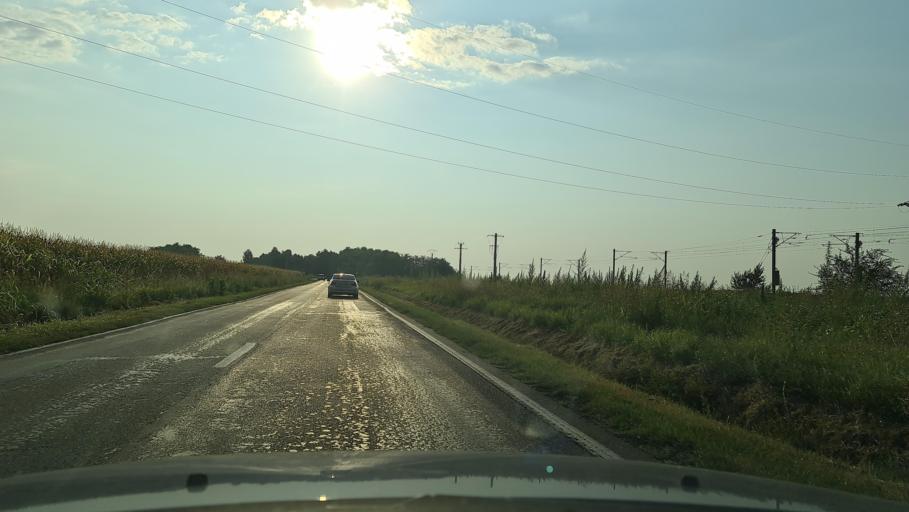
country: RO
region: Calarasi
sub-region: Oras Lehliu Gara
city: Razvani
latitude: 44.4369
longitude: 26.8852
